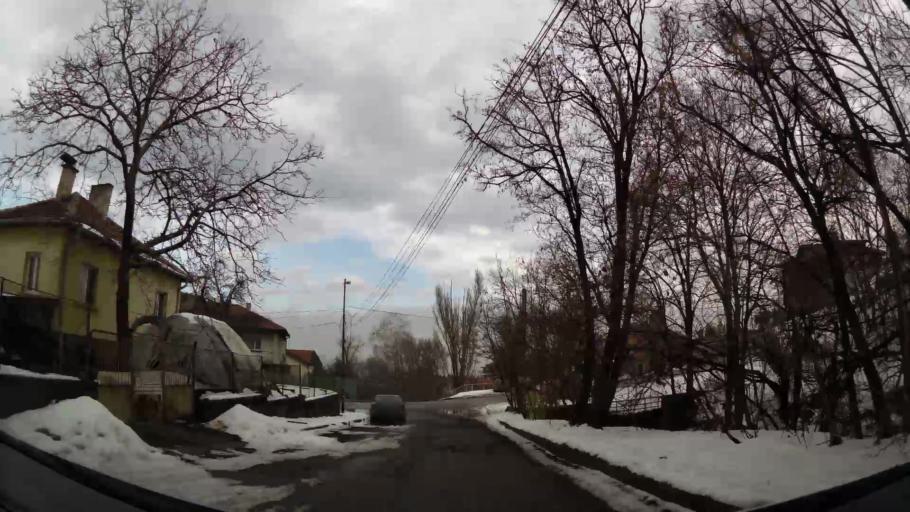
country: BG
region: Sofia-Capital
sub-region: Stolichna Obshtina
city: Sofia
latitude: 42.6476
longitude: 23.2654
